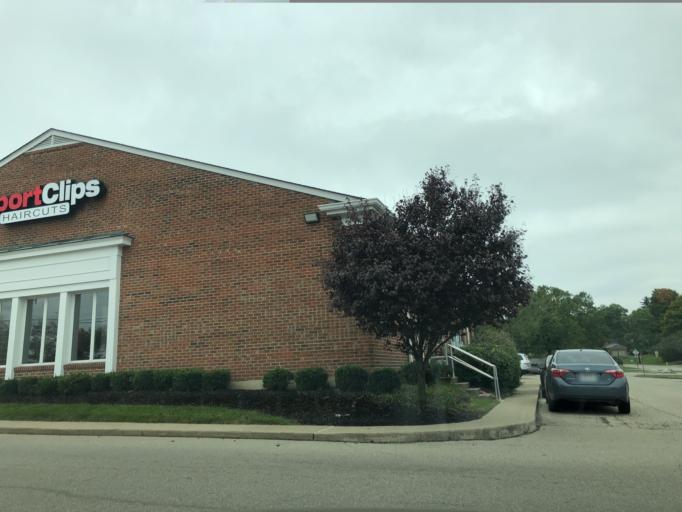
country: US
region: Ohio
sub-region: Hamilton County
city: Montgomery
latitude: 39.2391
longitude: -84.3496
